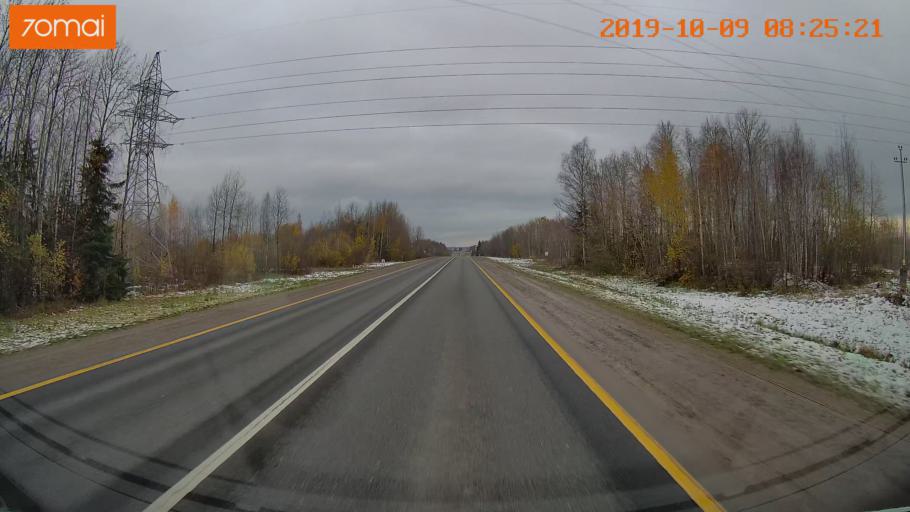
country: RU
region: Vologda
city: Gryazovets
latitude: 58.7798
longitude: 40.2728
